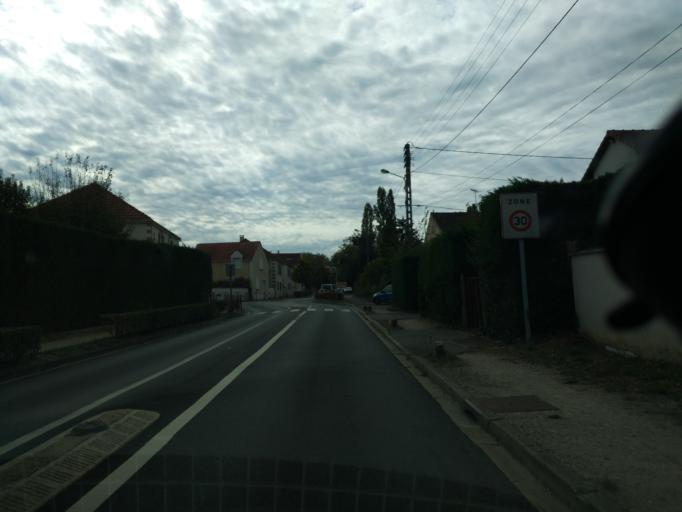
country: FR
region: Ile-de-France
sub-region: Departement de l'Essonne
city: Les Molieres
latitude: 48.6756
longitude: 2.0709
